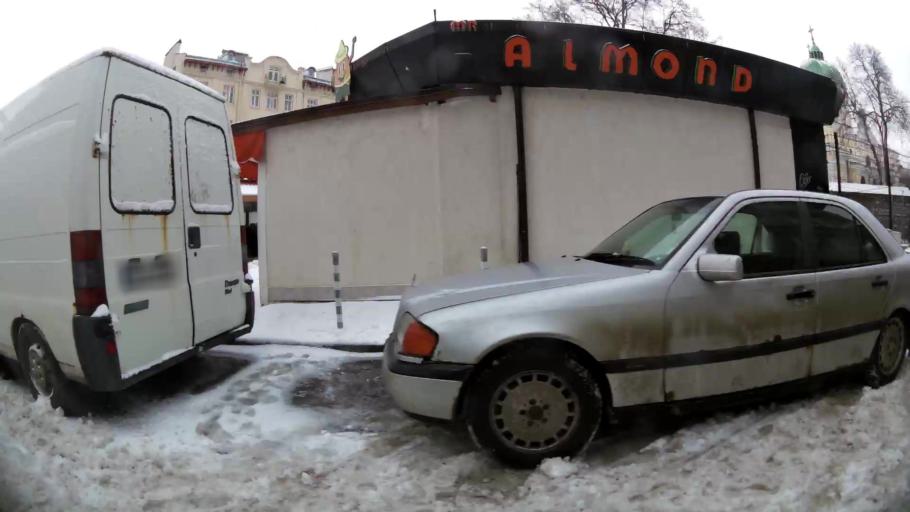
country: BG
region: Sofia-Capital
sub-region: Stolichna Obshtina
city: Sofia
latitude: 42.7032
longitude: 23.3209
